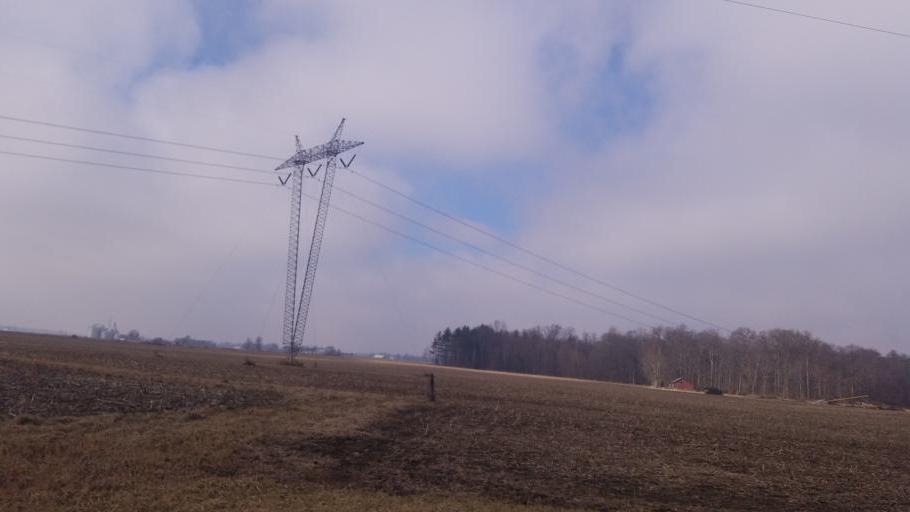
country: US
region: Ohio
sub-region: Crawford County
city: Galion
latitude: 40.7267
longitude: -82.8904
